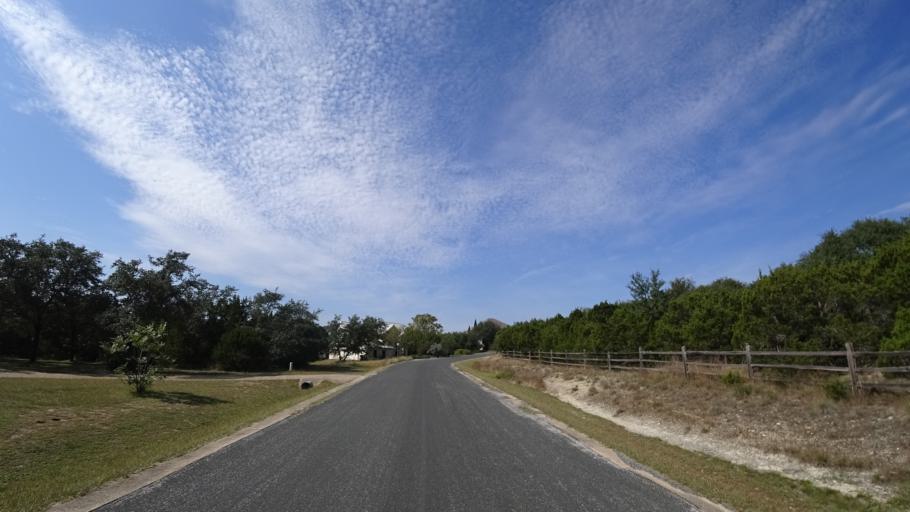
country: US
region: Texas
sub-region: Travis County
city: Bee Cave
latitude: 30.2236
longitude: -97.9383
